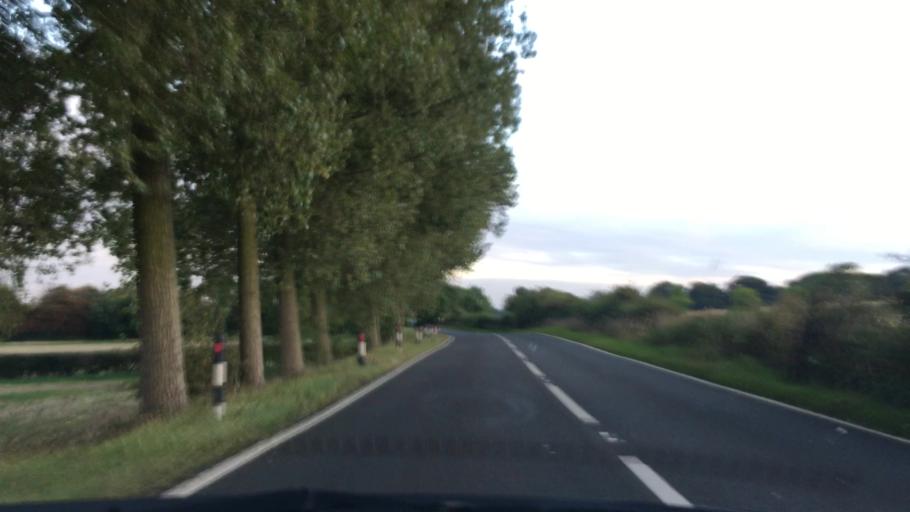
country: GB
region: England
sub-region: North East Lincolnshire
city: Wold Newton
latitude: 53.4675
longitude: -0.1053
